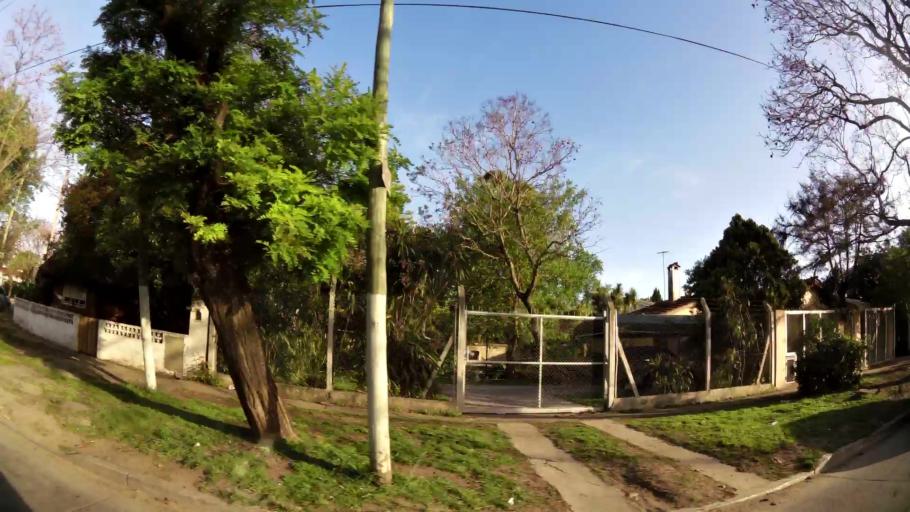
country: AR
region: Buenos Aires
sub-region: Partido de Quilmes
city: Quilmes
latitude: -34.7862
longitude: -58.2107
